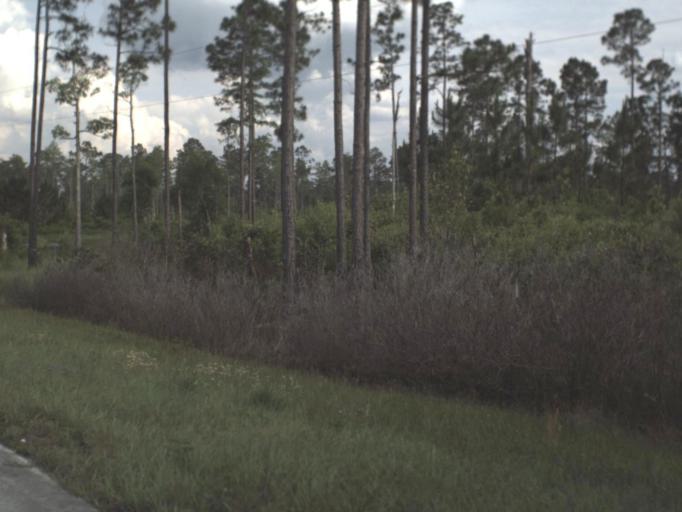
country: US
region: Florida
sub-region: Baker County
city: Macclenny
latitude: 30.5201
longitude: -82.2859
